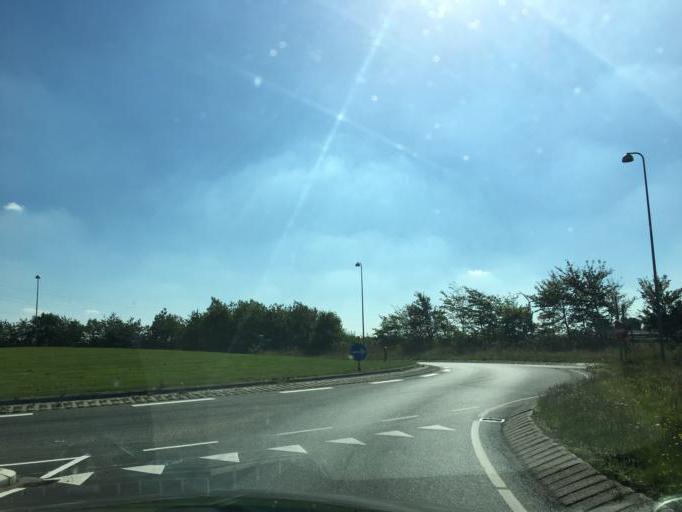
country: DK
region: South Denmark
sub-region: Kolding Kommune
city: Lunderskov
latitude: 55.5034
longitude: 9.2775
